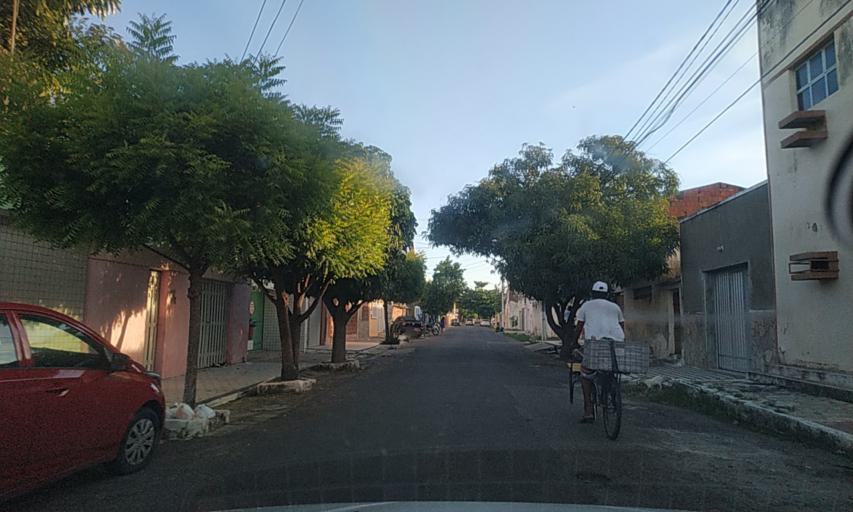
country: BR
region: Rio Grande do Norte
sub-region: Mossoro
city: Mossoro
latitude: -5.1921
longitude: -37.3390
